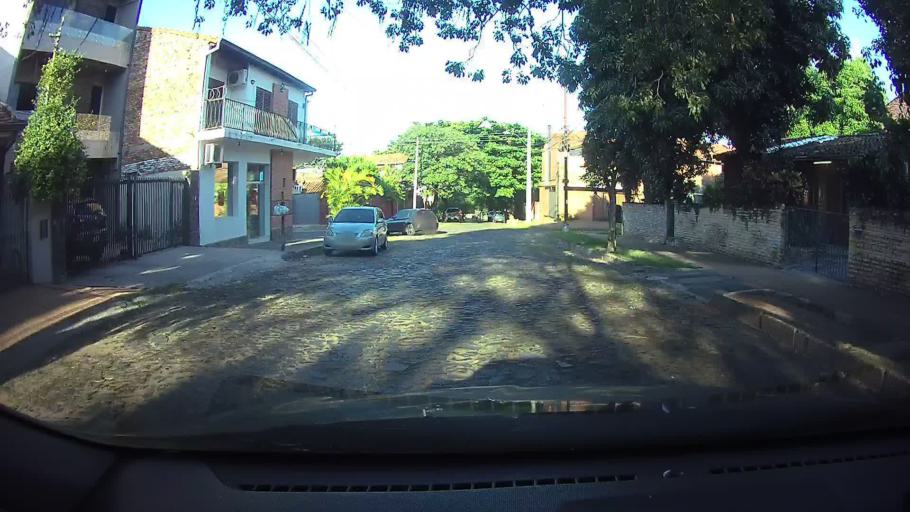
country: PY
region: Asuncion
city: Asuncion
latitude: -25.2804
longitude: -57.6022
